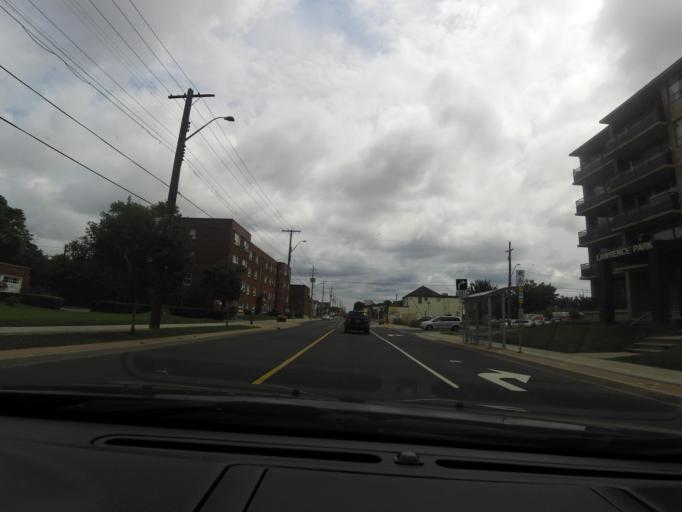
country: CA
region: Ontario
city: Hamilton
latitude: 43.2430
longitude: -79.8601
